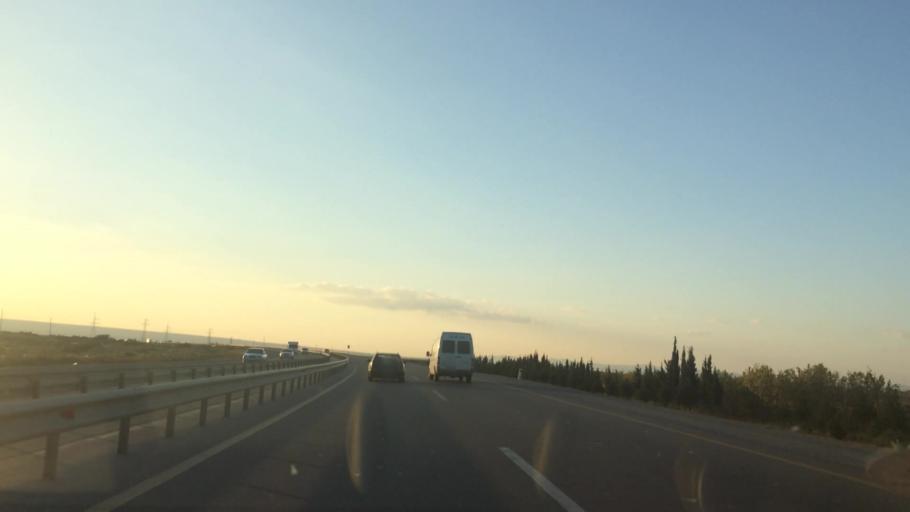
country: AZ
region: Baki
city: Qobustan
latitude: 39.9820
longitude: 49.2331
